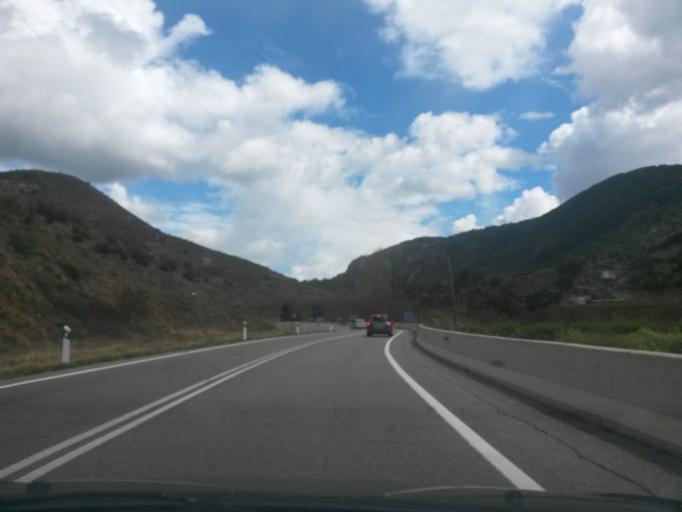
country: ES
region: Catalonia
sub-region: Provincia de Lleida
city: Toloriu
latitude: 42.3642
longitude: 1.6527
